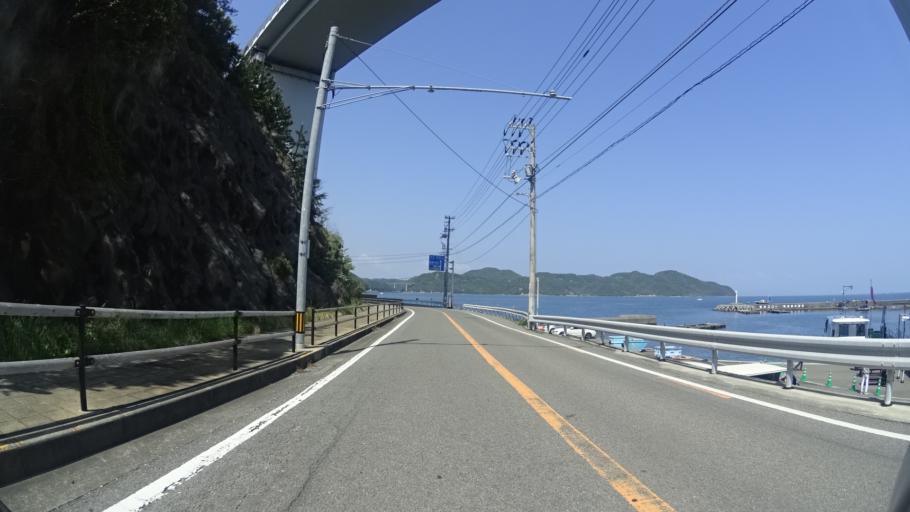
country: JP
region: Tokushima
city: Narutocho-mitsuishi
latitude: 34.2334
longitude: 134.6373
